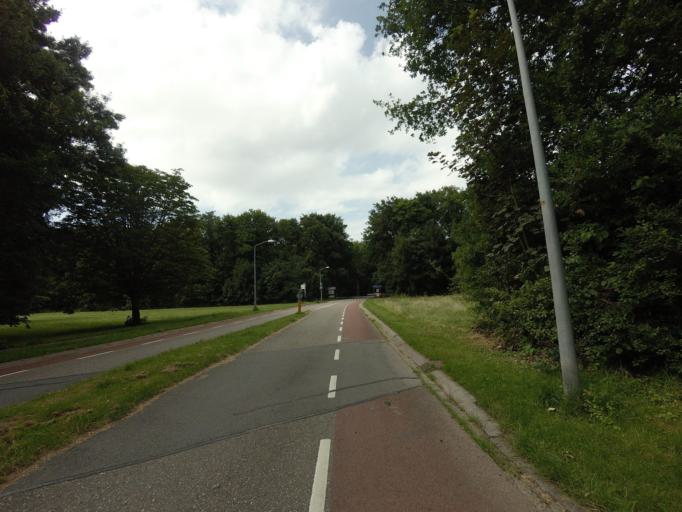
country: NL
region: North Holland
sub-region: Gemeente Huizen
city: Huizen
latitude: 52.3437
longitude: 5.2977
